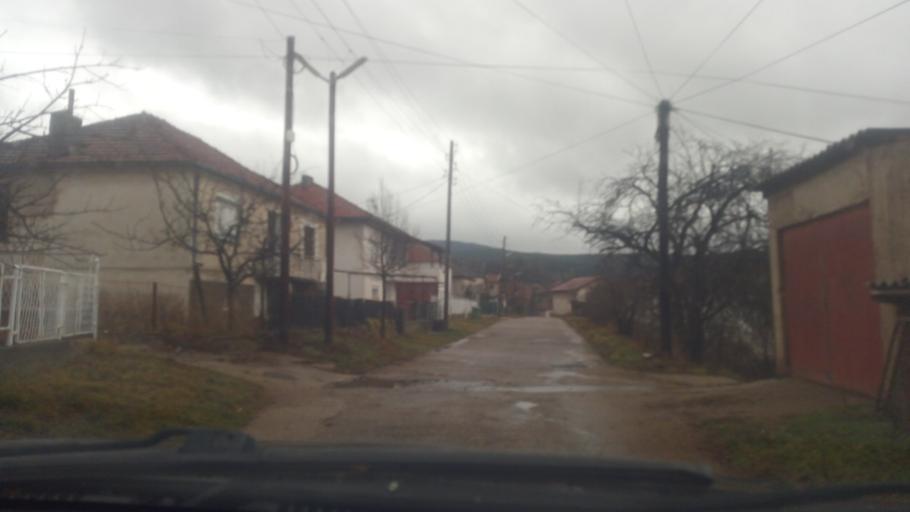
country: MK
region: Pehcevo
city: Pehcevo
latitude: 41.7638
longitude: 22.8868
